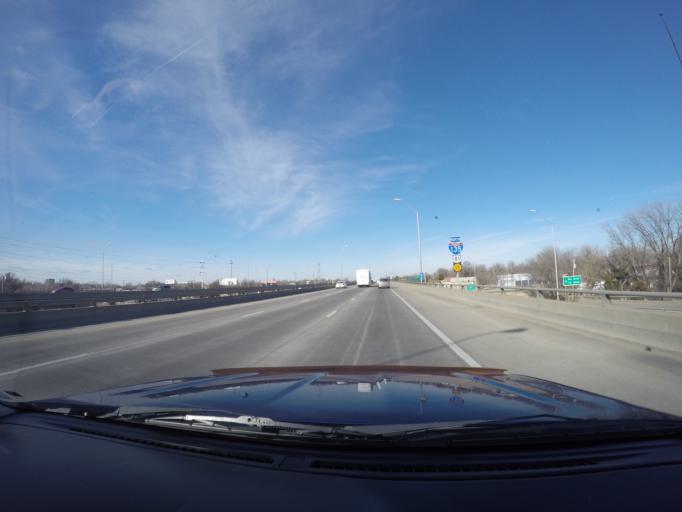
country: US
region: Kansas
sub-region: Sedgwick County
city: Wichita
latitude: 37.6870
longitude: -97.3130
